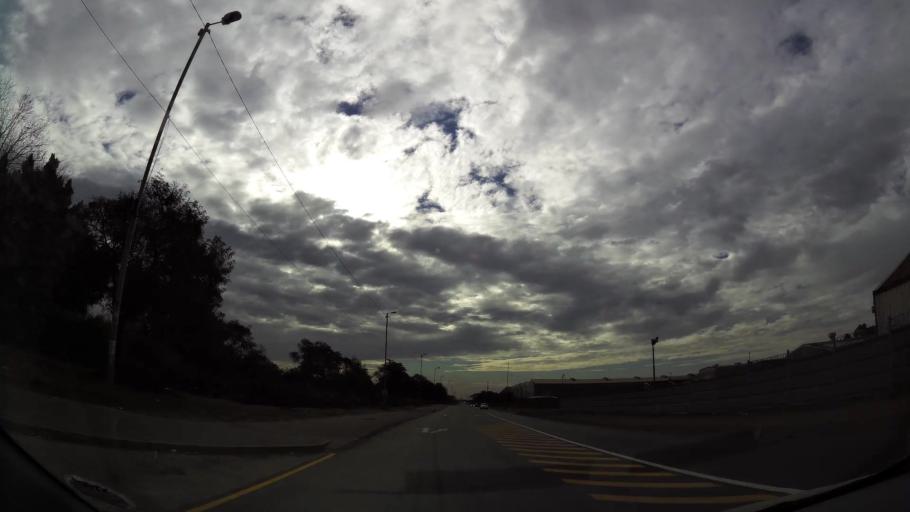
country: ZA
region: Gauteng
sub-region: City of Tshwane Metropolitan Municipality
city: Pretoria
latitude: -25.7247
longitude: 28.3118
